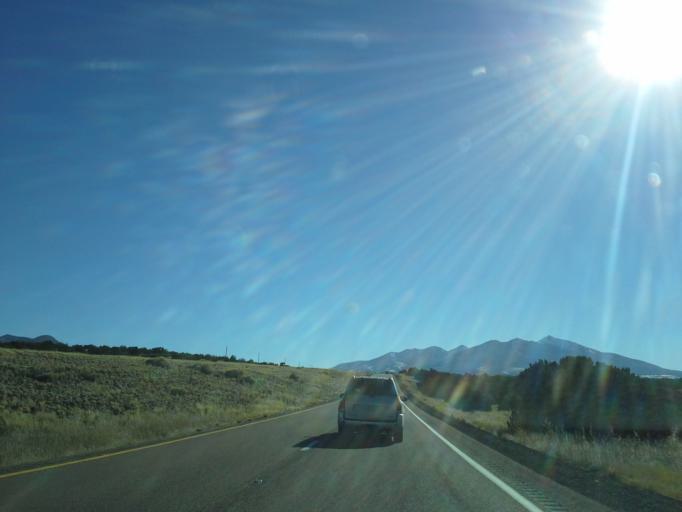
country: US
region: Arizona
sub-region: Coconino County
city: Flagstaff
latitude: 35.5065
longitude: -111.5486
